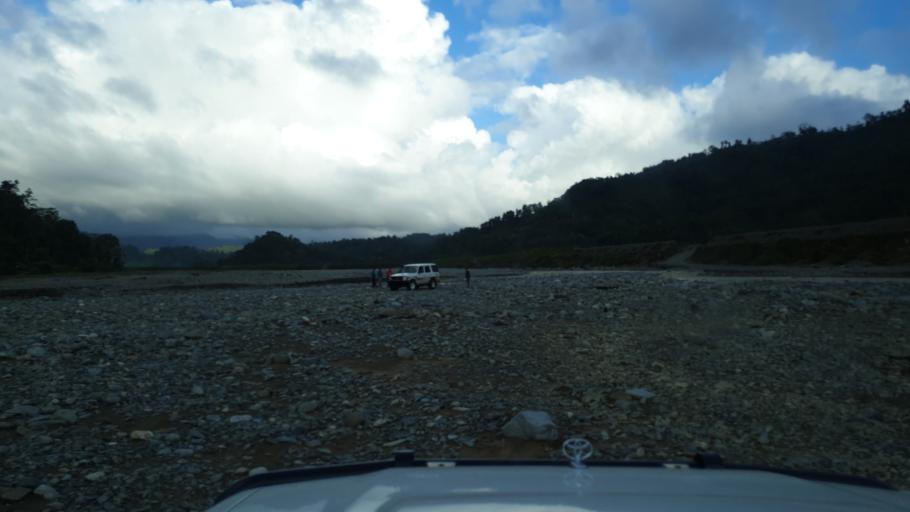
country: PG
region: Bougainville
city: Panguna
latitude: -6.3785
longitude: 155.4196
